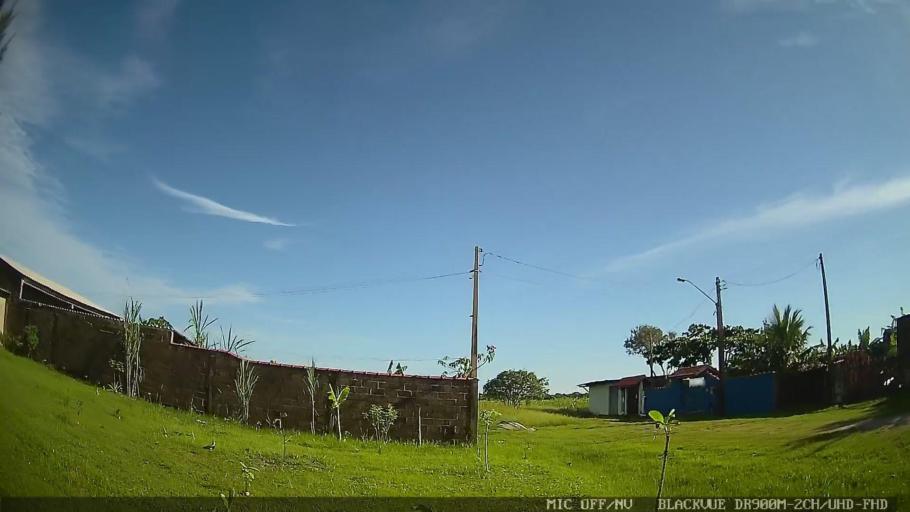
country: BR
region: Sao Paulo
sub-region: Iguape
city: Iguape
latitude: -24.7635
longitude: -47.5777
